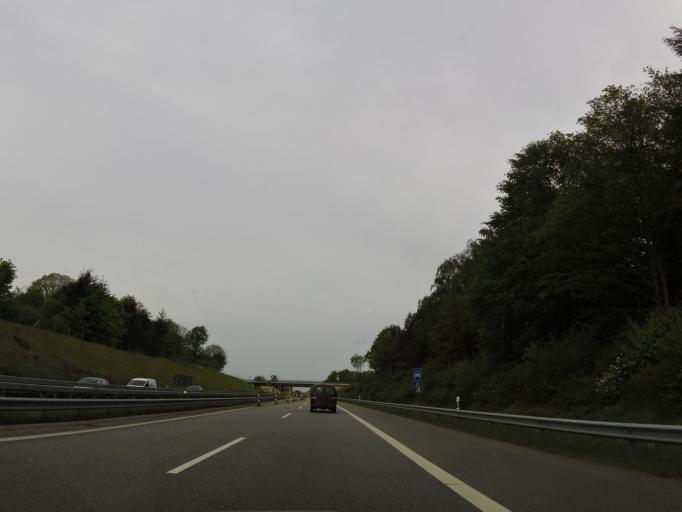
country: DE
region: Schleswig-Holstein
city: Itzehoe
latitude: 53.8982
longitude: 9.5098
